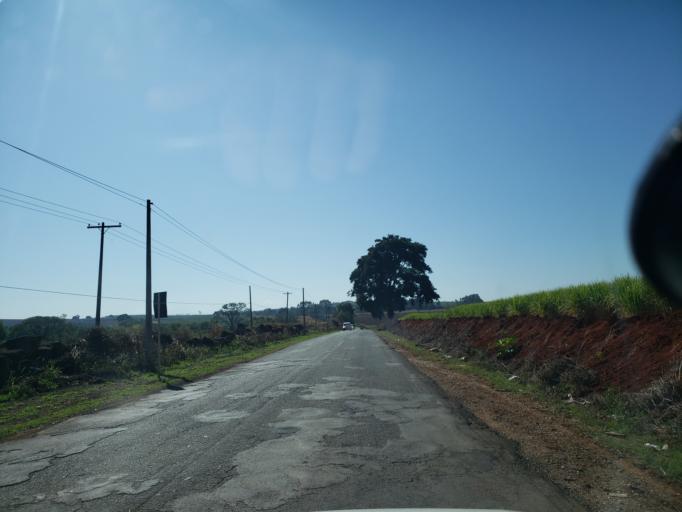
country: BR
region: Sao Paulo
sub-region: Moji-Guacu
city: Mogi-Gaucu
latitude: -22.3535
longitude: -46.9008
